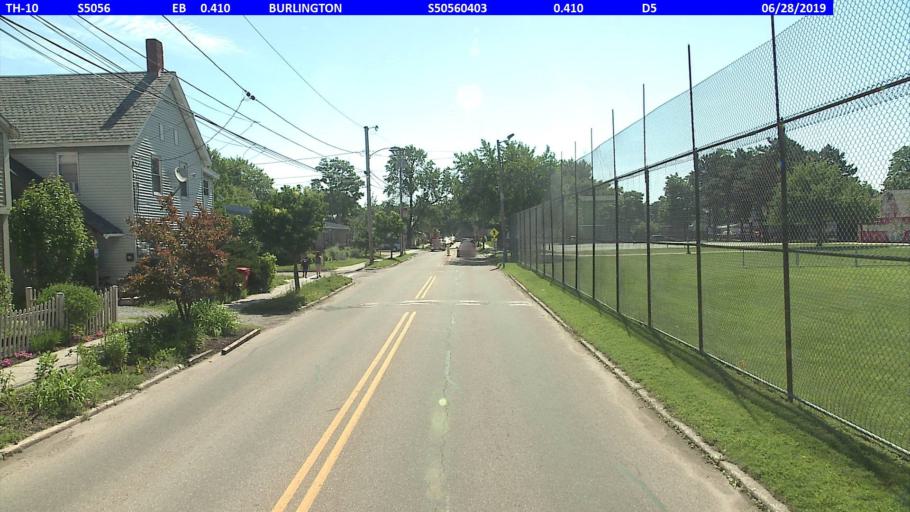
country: US
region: Vermont
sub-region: Chittenden County
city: Burlington
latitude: 44.4899
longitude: -73.2121
